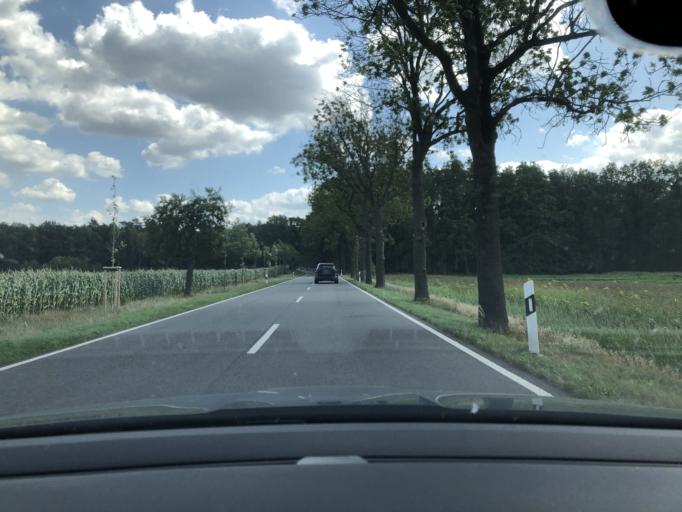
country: DE
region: Brandenburg
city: Wittstock
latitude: 53.0749
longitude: 12.5076
